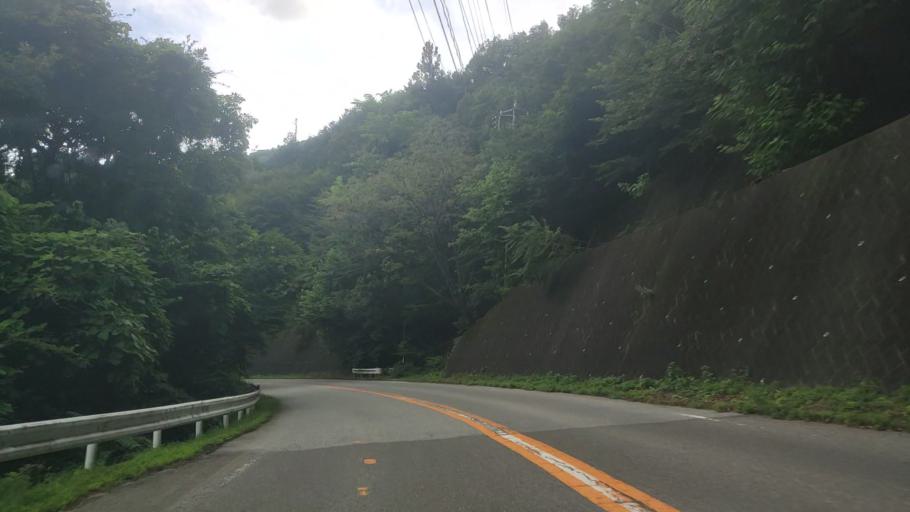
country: JP
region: Gunma
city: Omamacho-omama
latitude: 36.6088
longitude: 139.4026
